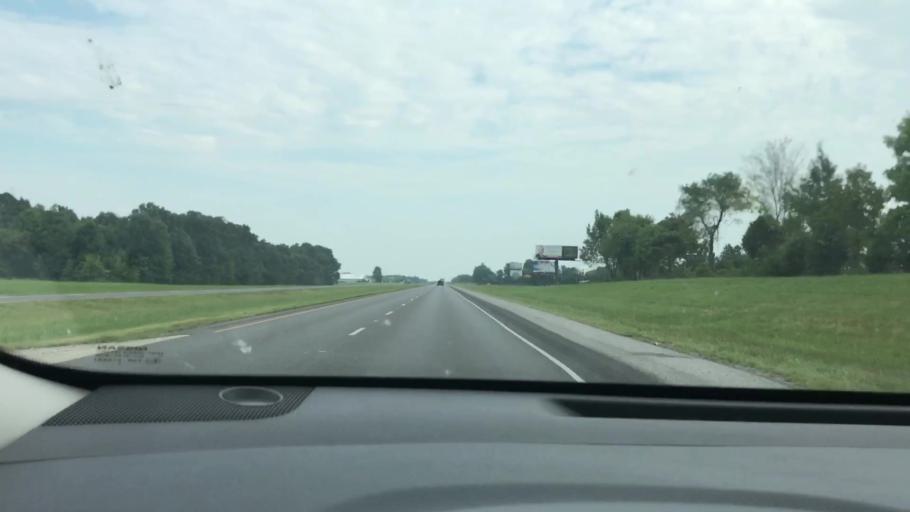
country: US
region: Kentucky
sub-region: Calloway County
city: Murray
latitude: 36.6831
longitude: -88.3027
